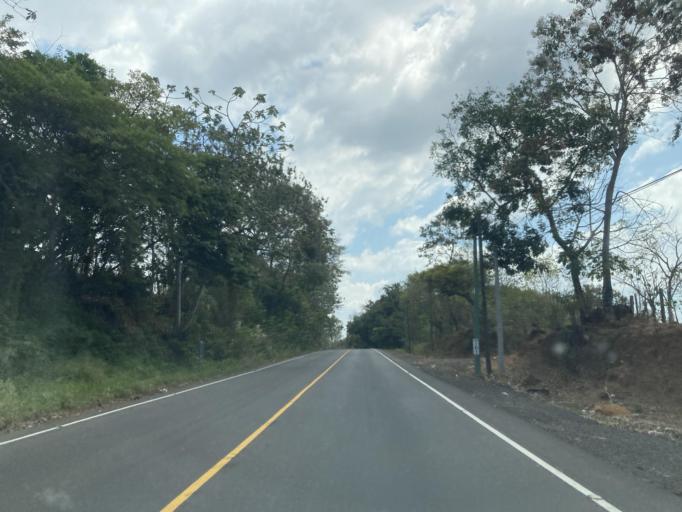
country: GT
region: Santa Rosa
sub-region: Municipio de Taxisco
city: Taxisco
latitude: 14.0894
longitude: -90.5060
